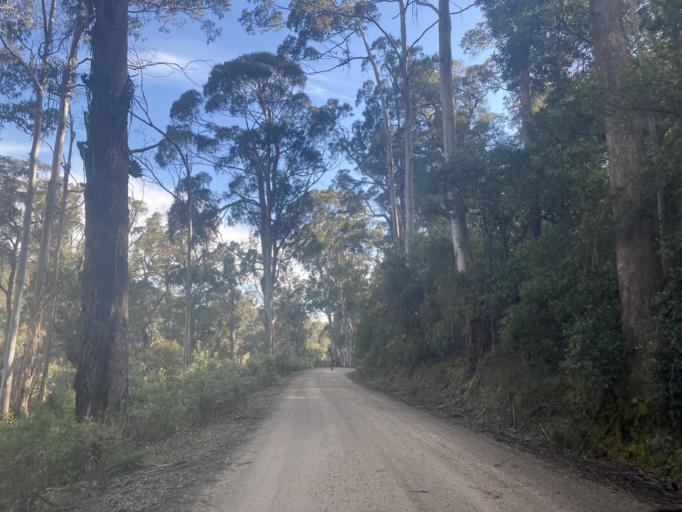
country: AU
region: Victoria
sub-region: Mansfield
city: Mansfield
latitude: -36.8436
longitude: 146.1731
